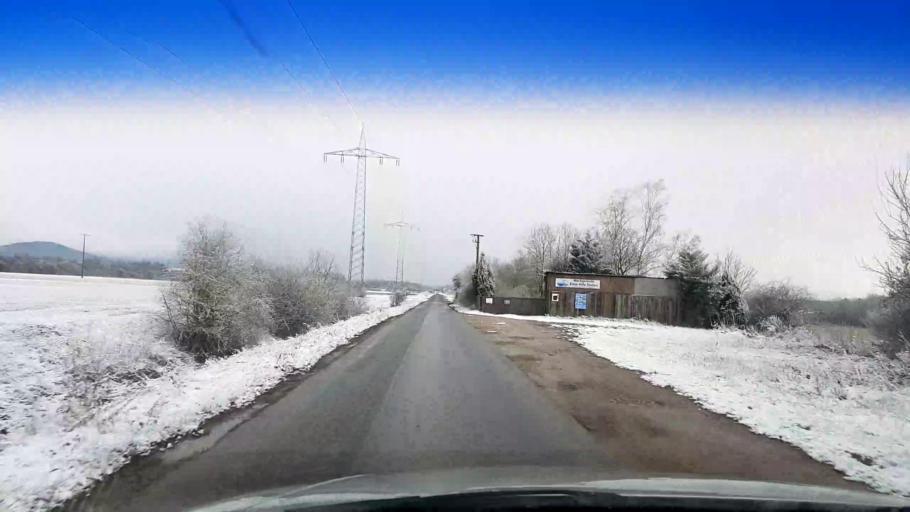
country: DE
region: Bavaria
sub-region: Upper Franconia
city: Altendorf
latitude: 49.8131
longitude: 11.0064
